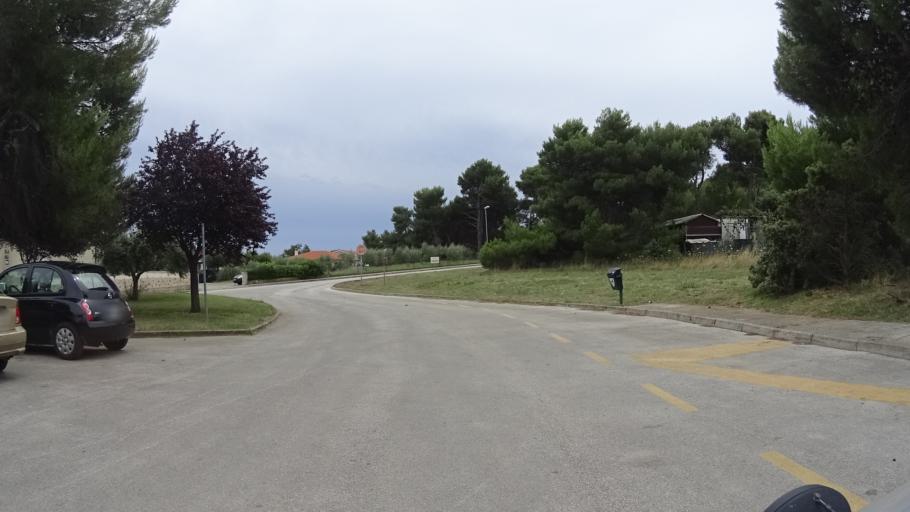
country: HR
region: Istarska
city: Medulin
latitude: 44.8055
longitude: 13.9089
